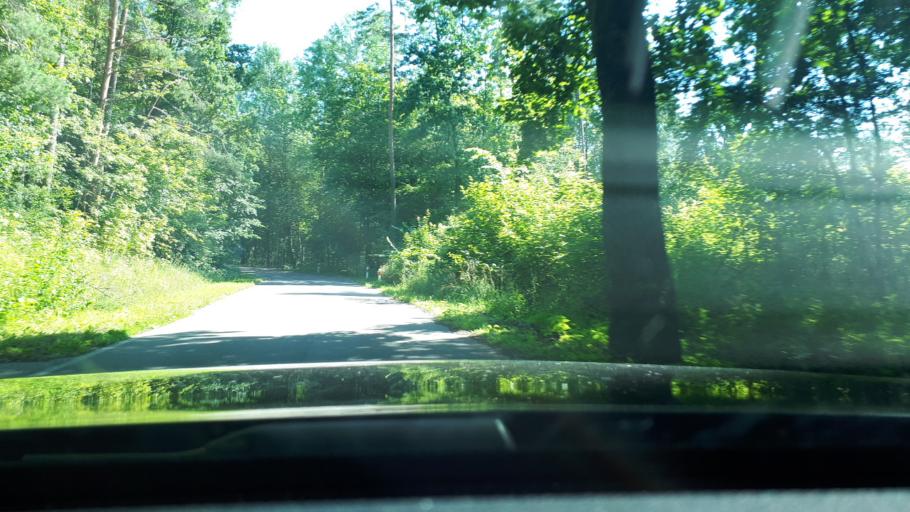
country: PL
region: Warmian-Masurian Voivodeship
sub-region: Powiat ostrodzki
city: Ostroda
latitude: 53.6831
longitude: 20.0720
